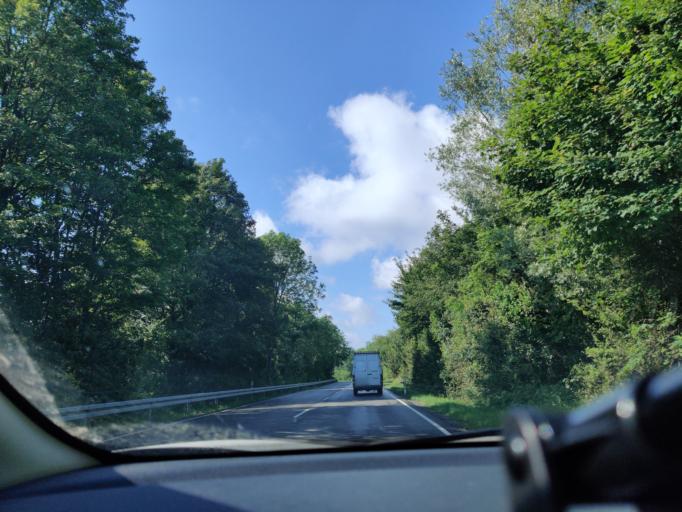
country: DE
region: Saarland
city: Gersheim
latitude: 49.1512
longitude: 7.1534
